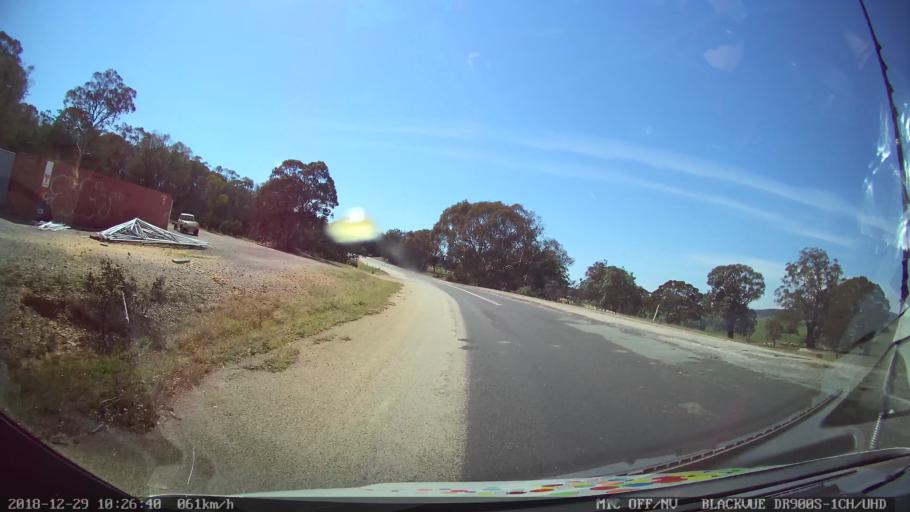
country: AU
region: New South Wales
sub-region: Yass Valley
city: Gundaroo
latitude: -34.9280
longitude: 149.4447
